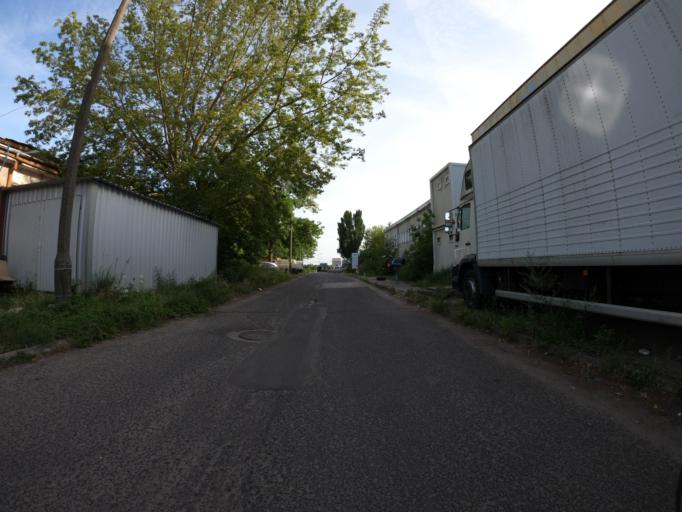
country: PL
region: West Pomeranian Voivodeship
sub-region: Powiat policki
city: Przeclaw
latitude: 53.4020
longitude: 14.5058
